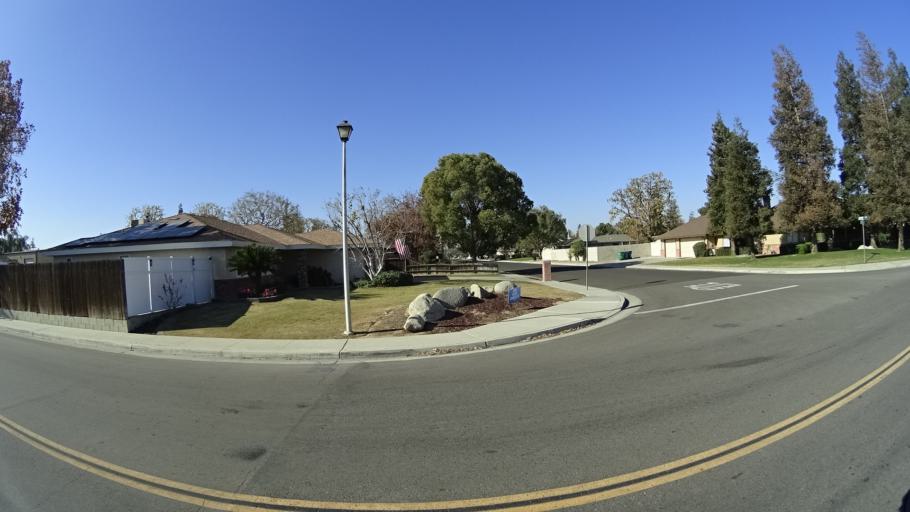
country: US
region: California
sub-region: Kern County
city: Rosedale
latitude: 35.3775
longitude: -119.1280
